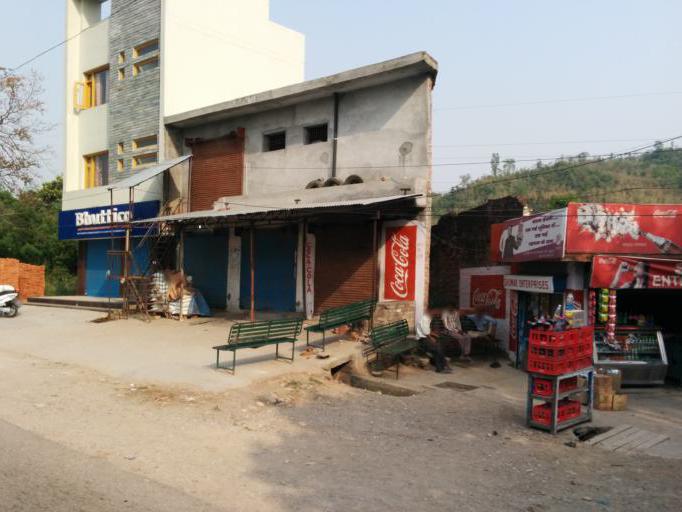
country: IN
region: Punjab
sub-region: Gurdaspur
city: Dharkalan
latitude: 32.2867
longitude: 75.8697
